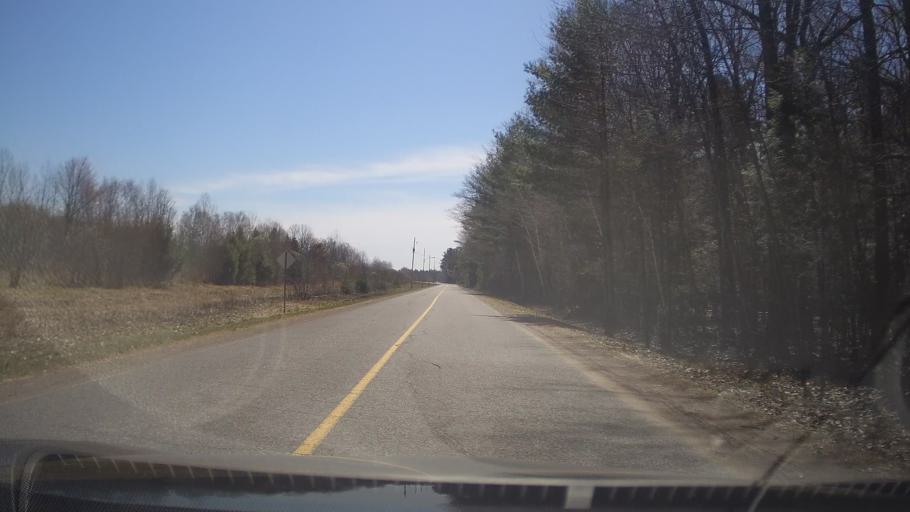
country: CA
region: Ontario
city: Arnprior
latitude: 45.5202
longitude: -76.4116
